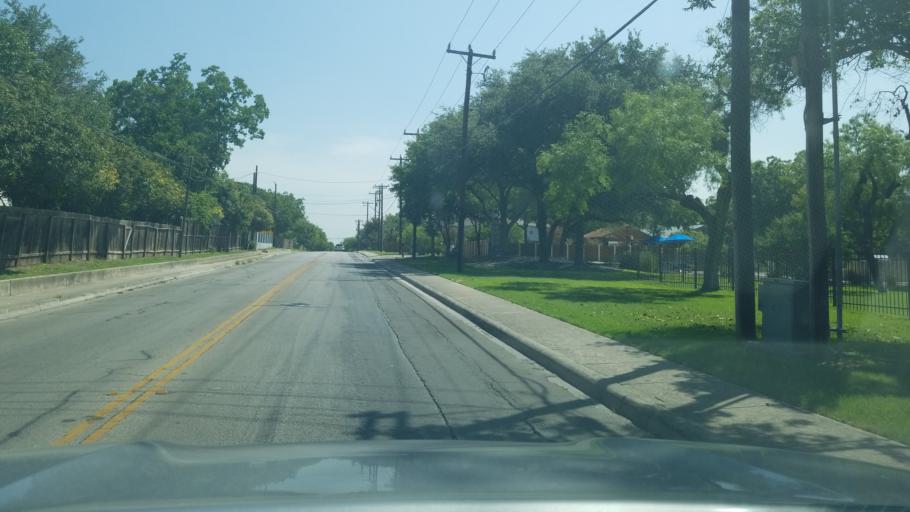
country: US
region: Texas
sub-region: Bexar County
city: Hollywood Park
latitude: 29.5705
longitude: -98.4730
